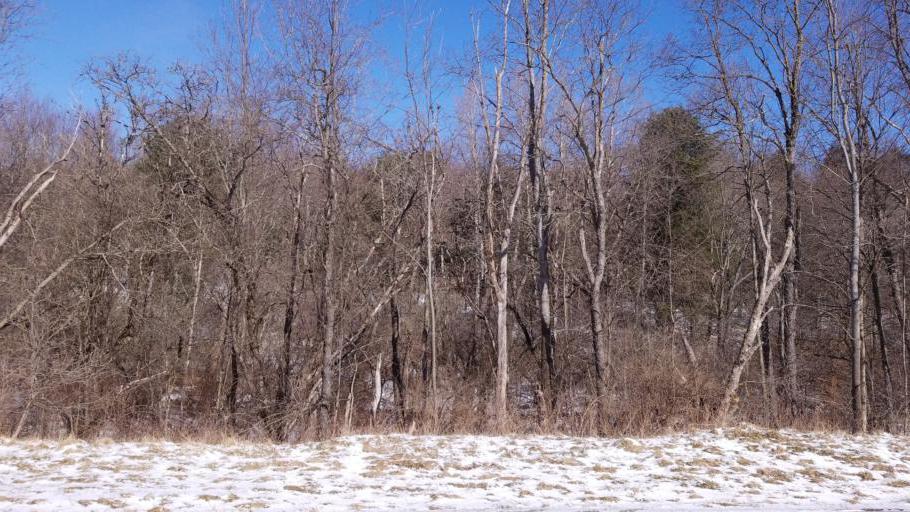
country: US
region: New York
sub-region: Allegany County
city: Andover
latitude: 42.0651
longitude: -77.8261
